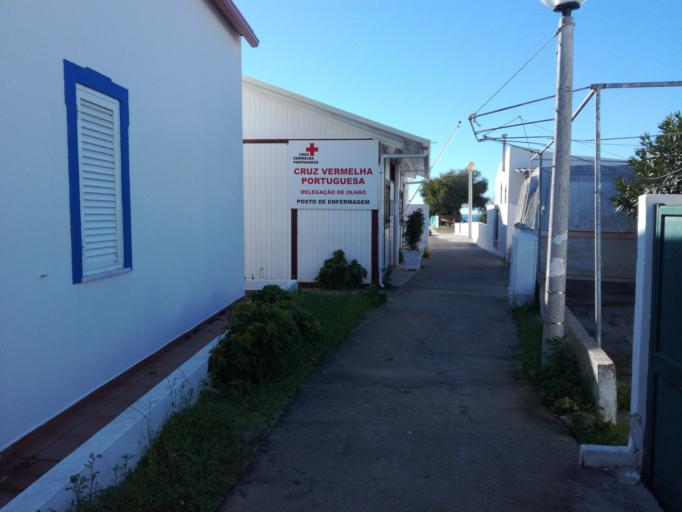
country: PT
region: Faro
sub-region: Olhao
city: Olhao
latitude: 37.0216
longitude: -7.8056
